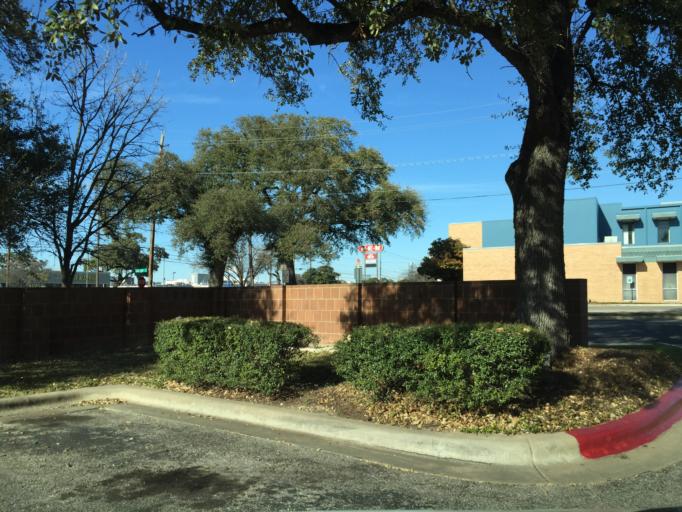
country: US
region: Texas
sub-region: Travis County
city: Austin
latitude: 30.2369
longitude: -97.7547
